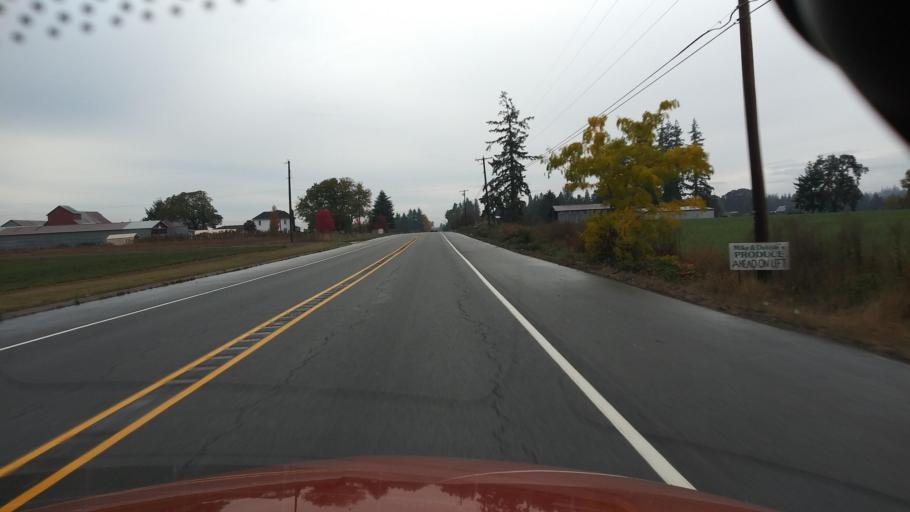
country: US
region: Oregon
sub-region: Washington County
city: Cornelius
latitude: 45.5337
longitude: -123.0597
